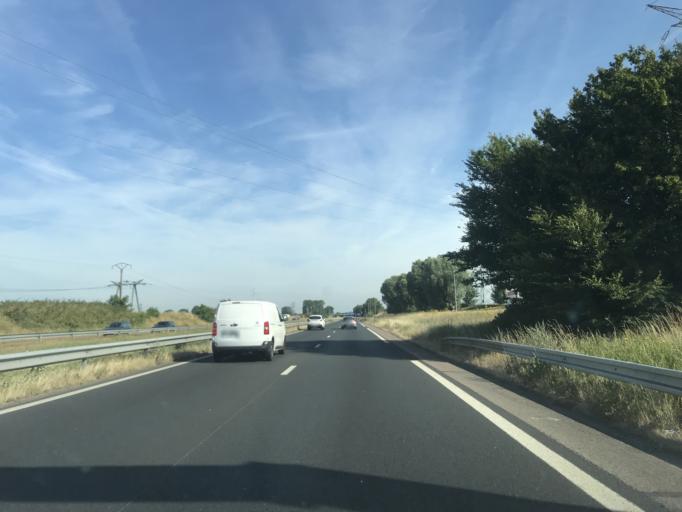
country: FR
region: Haute-Normandie
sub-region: Departement de la Seine-Maritime
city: La Vaupaliere
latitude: 49.4950
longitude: 0.9972
